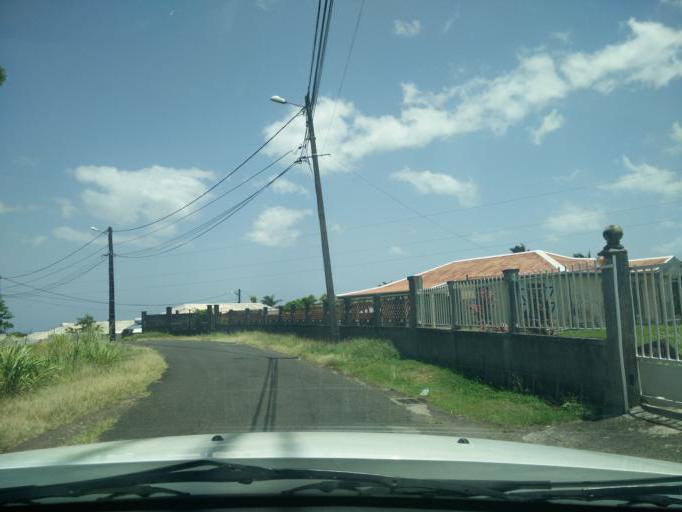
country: GP
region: Guadeloupe
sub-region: Guadeloupe
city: Basse-Terre
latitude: 15.9877
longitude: -61.7116
